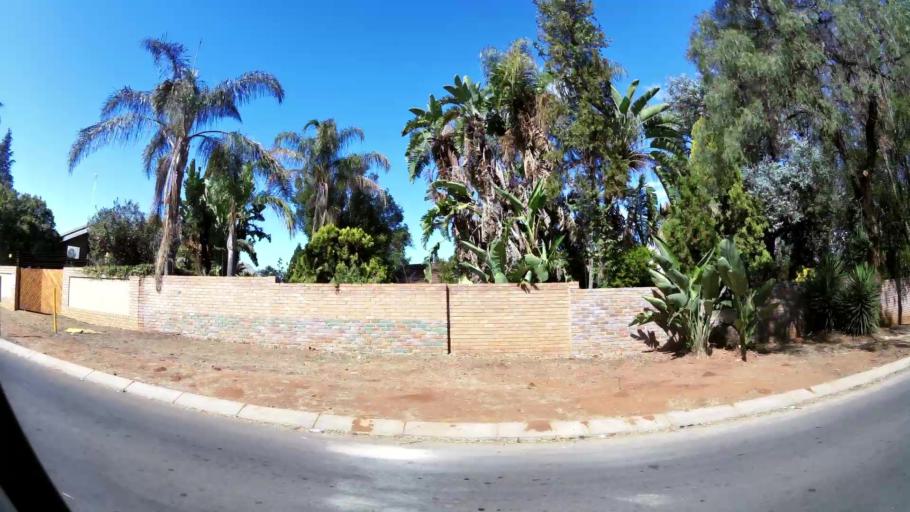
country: ZA
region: Limpopo
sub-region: Capricorn District Municipality
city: Polokwane
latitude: -23.9105
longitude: 29.4874
